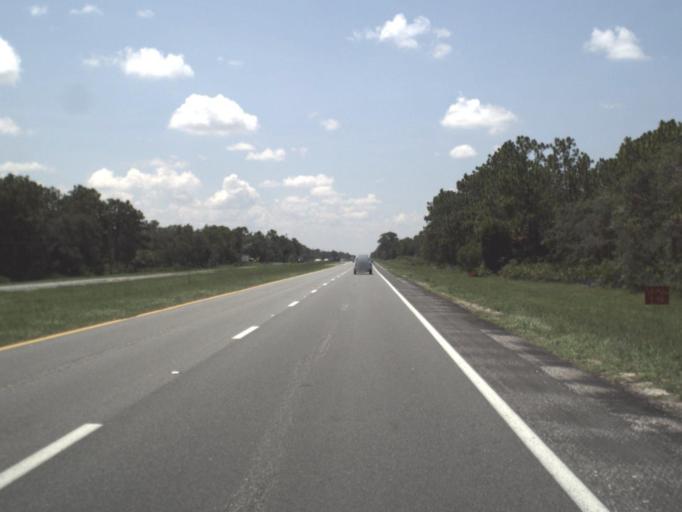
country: US
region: Florida
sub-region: Citrus County
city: Sugarmill Woods
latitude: 28.6865
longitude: -82.5526
